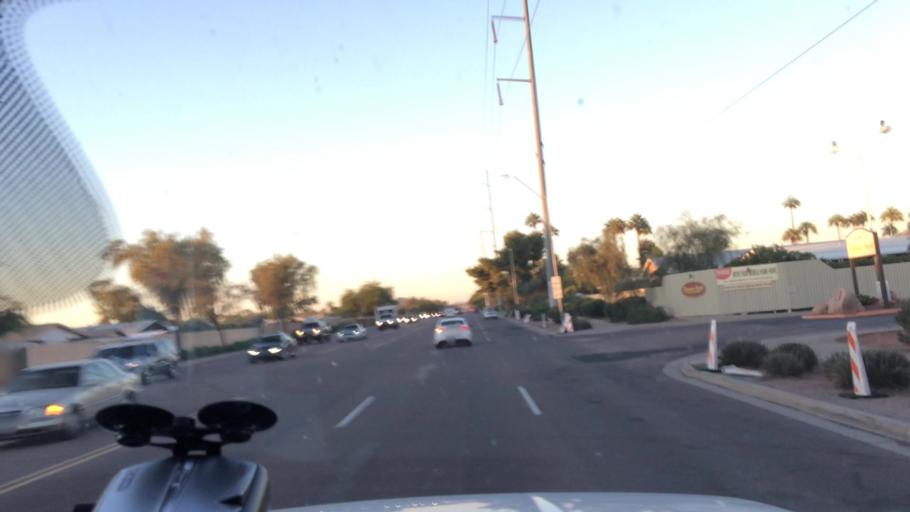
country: US
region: Arizona
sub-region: Maricopa County
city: Glendale
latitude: 33.6483
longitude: -112.0655
